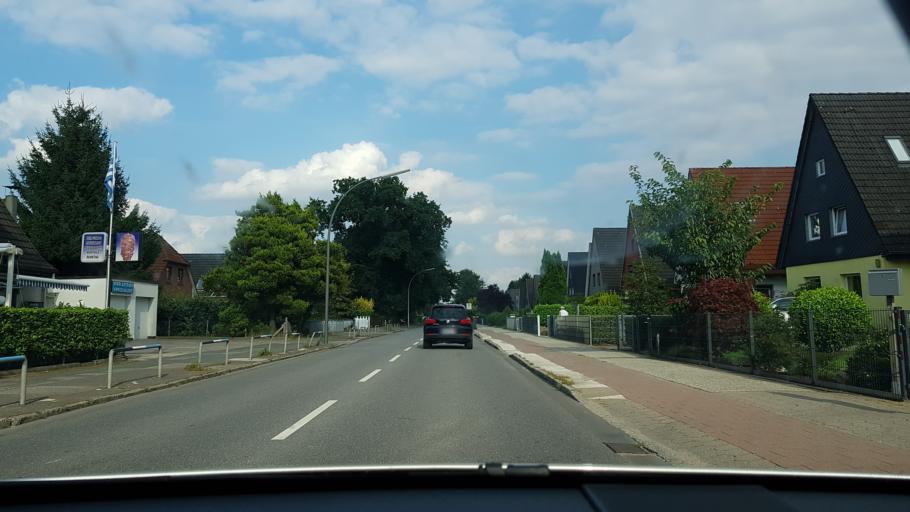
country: DE
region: Hamburg
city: Farmsen-Berne
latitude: 53.6209
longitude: 10.1025
